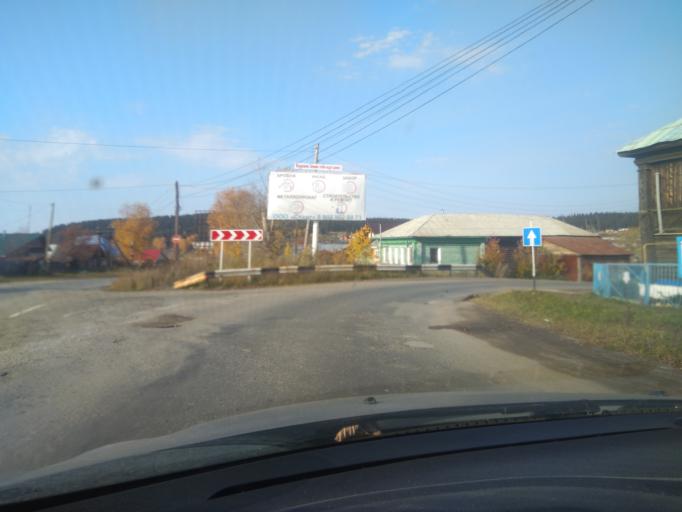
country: RU
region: Sverdlovsk
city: Nizhniye Sergi
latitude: 56.6762
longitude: 59.3358
